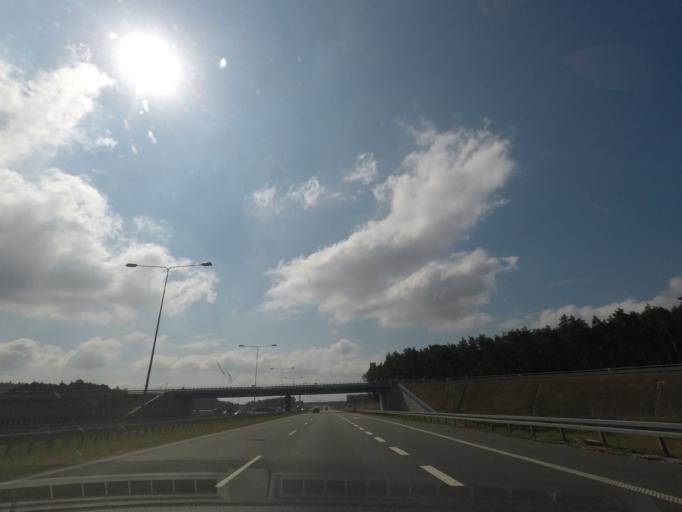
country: PL
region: Kujawsko-Pomorskie
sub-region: Powiat aleksandrowski
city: Aleksandrow Kujawski
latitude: 52.9052
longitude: 18.7205
